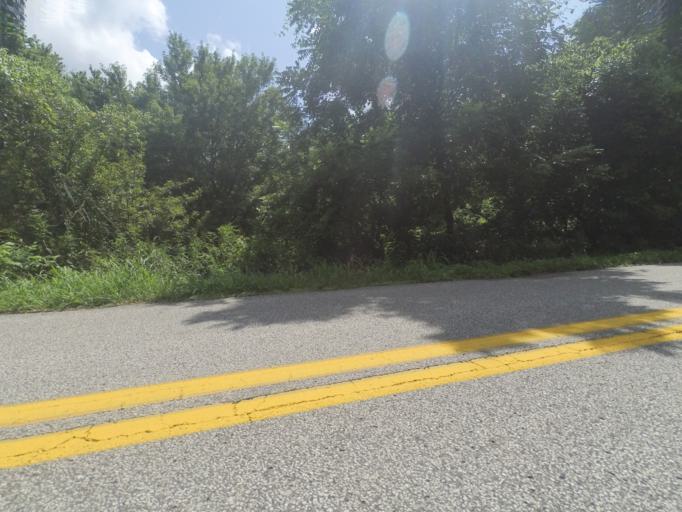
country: US
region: West Virginia
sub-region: Cabell County
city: Pea Ridge
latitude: 38.4283
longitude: -82.3065
